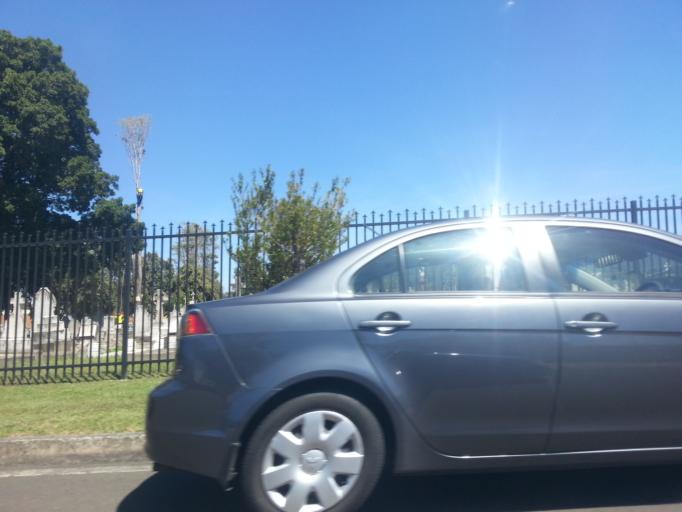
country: AU
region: New South Wales
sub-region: Wollongong
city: Wollongong
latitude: -34.4358
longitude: 150.8906
